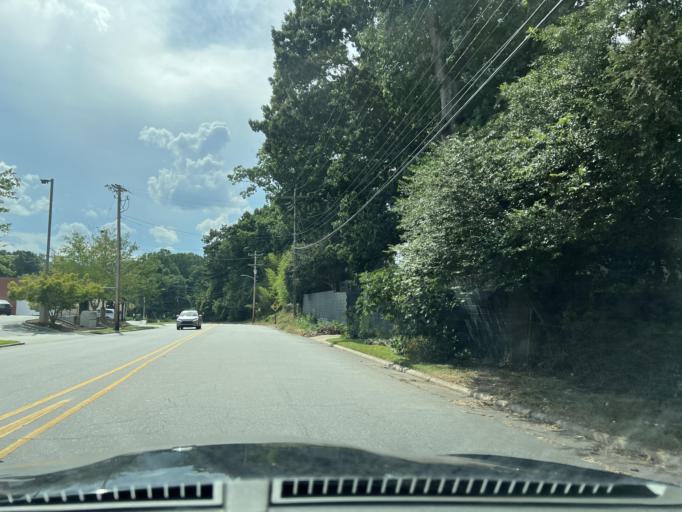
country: US
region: North Carolina
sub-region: Iredell County
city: Statesville
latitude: 35.7954
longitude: -80.8741
